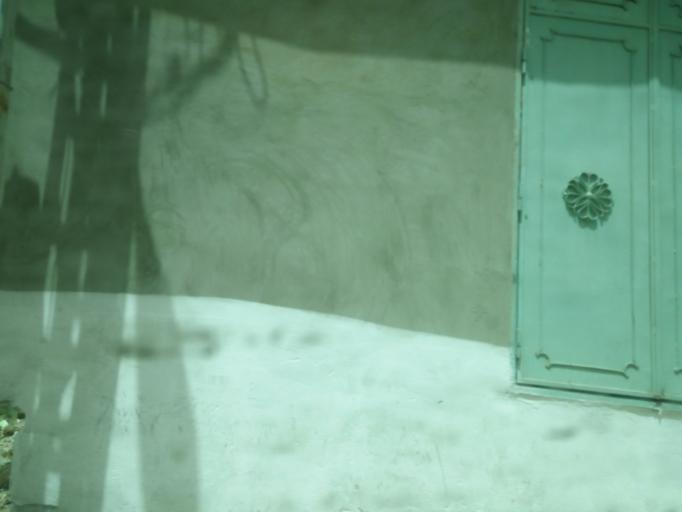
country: DZ
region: Ghardaia
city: Ghardaia
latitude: 32.4855
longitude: 3.6397
